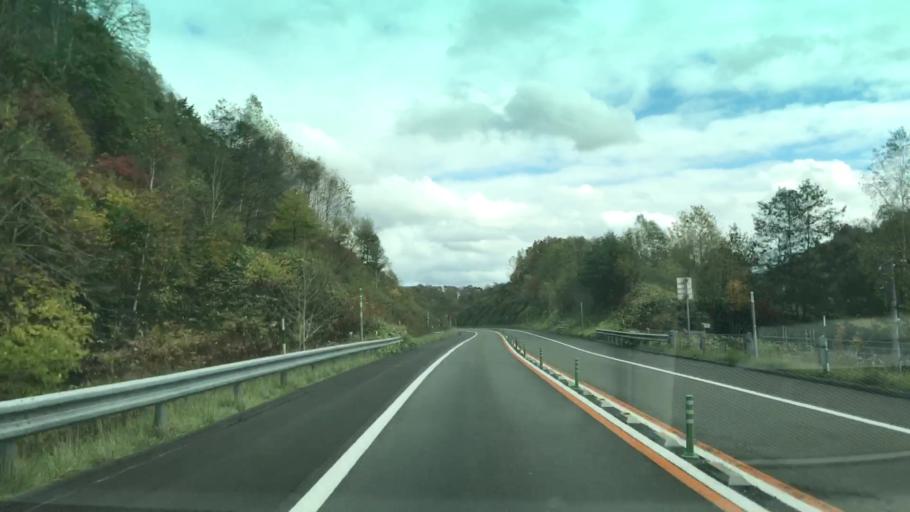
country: JP
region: Hokkaido
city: Chitose
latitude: 42.9173
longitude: 141.9604
